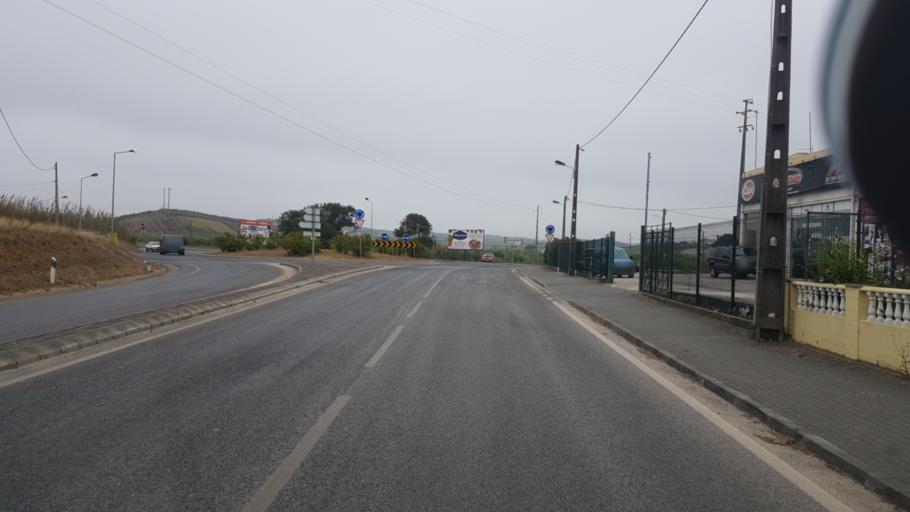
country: PT
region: Lisbon
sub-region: Torres Vedras
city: Silveira
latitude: 39.0897
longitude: -9.3350
